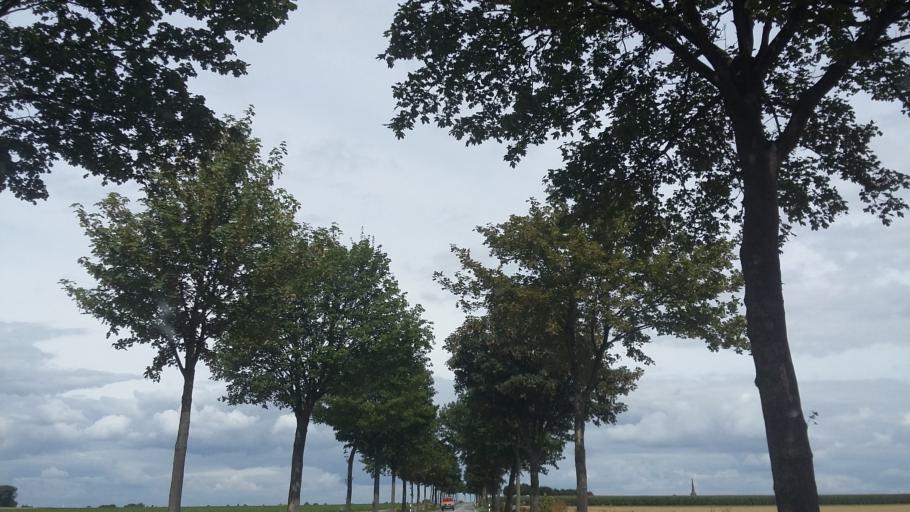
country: DE
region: Lower Saxony
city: Harsum
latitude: 52.1910
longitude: 10.0076
